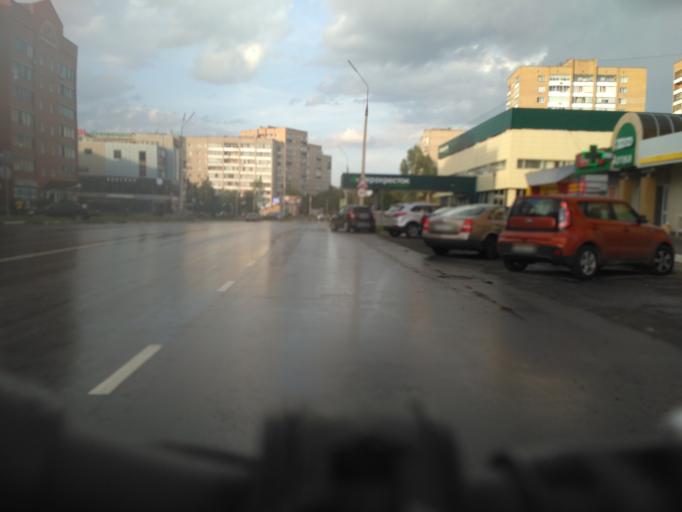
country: RU
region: Moskovskaya
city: Dubna
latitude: 56.7382
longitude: 37.1671
